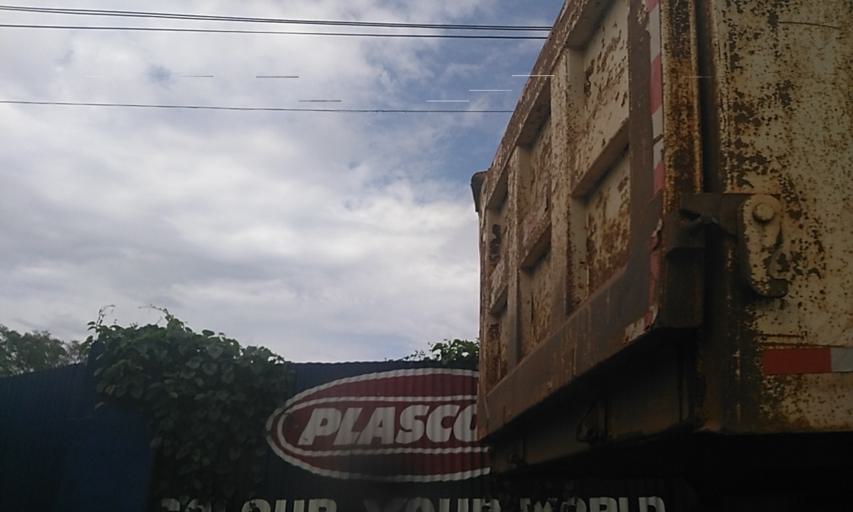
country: UG
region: Central Region
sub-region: Kampala District
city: Kampala
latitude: 0.3233
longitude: 32.5953
